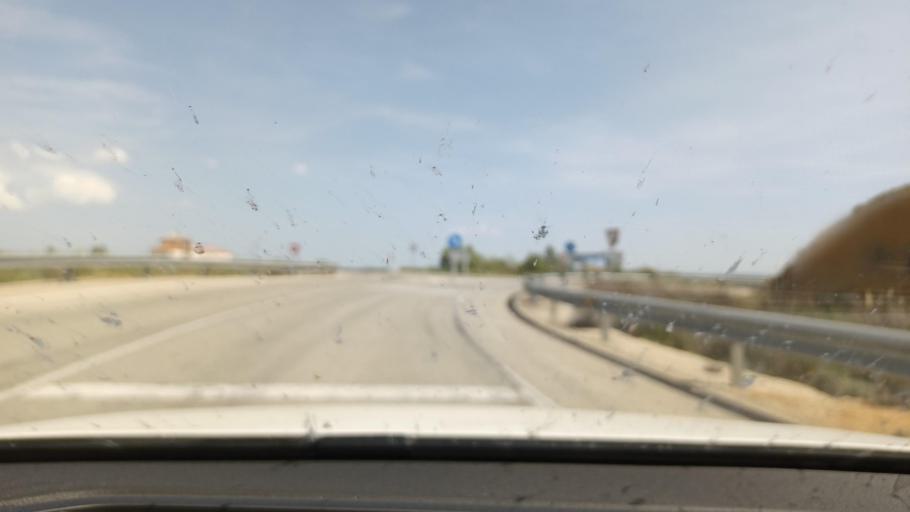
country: ES
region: Aragon
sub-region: Provincia de Zaragoza
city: Monreal de Ariza
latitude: 41.3089
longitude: -2.1261
